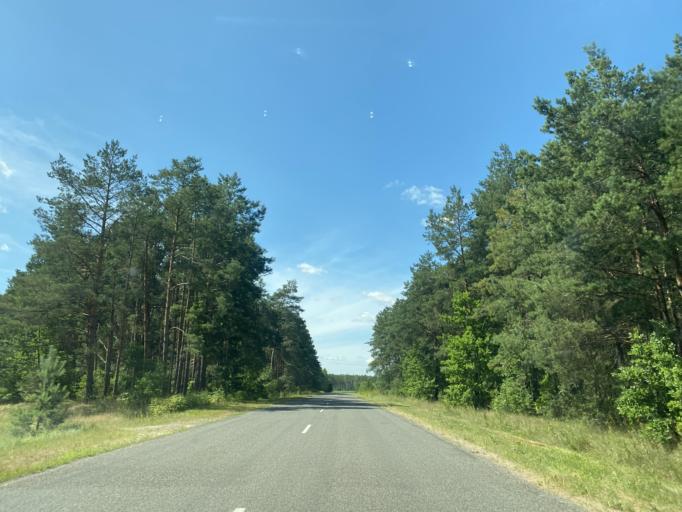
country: BY
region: Brest
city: Ivanava
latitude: 52.2244
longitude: 25.6350
